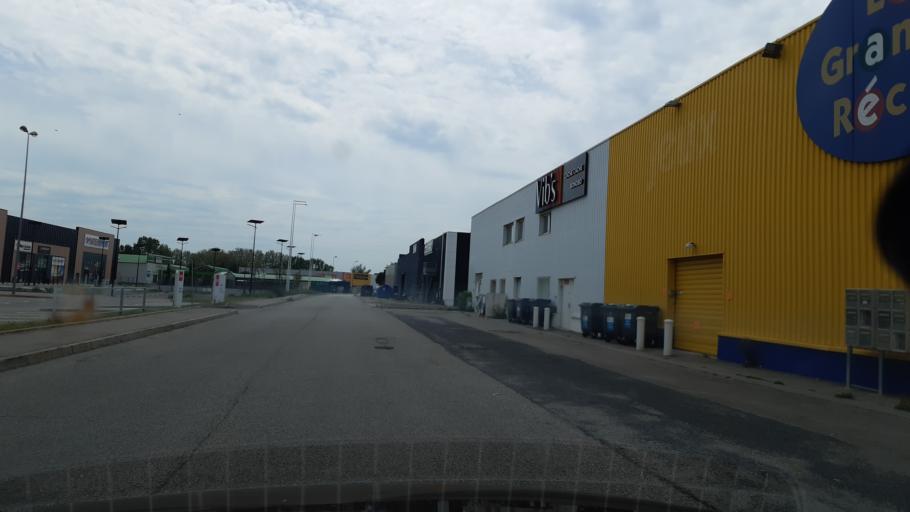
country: FR
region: Languedoc-Roussillon
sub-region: Departement de l'Aude
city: Narbonne
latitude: 43.1777
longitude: 3.0302
